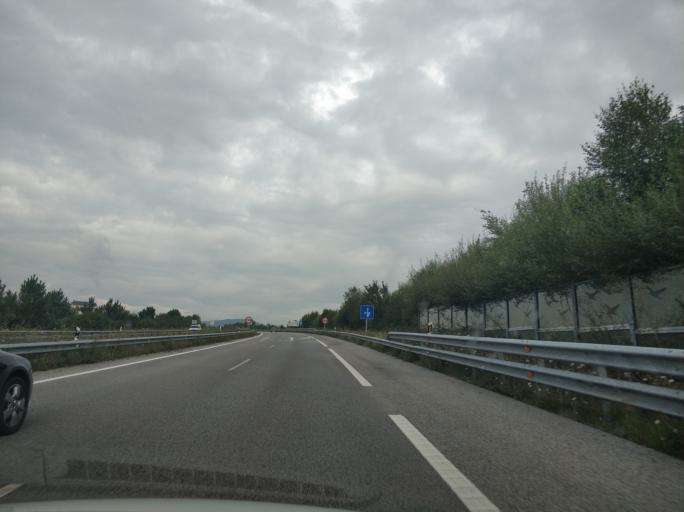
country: ES
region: Asturias
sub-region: Province of Asturias
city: Navia
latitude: 43.5337
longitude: -6.6822
